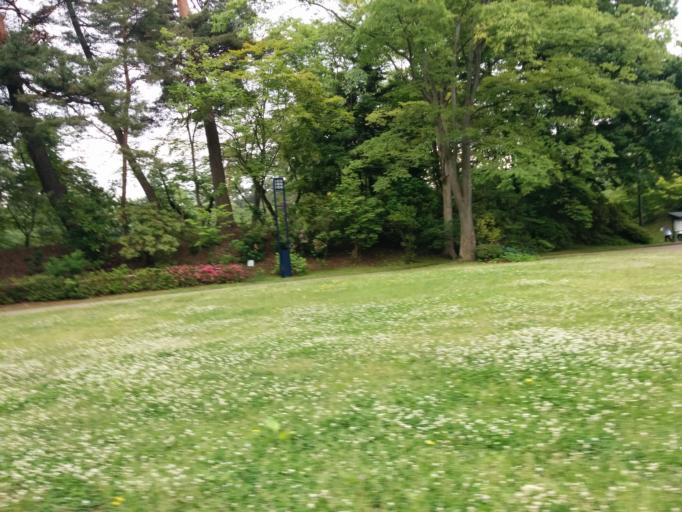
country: JP
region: Aomori
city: Hirosaki
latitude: 40.6098
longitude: 140.4647
